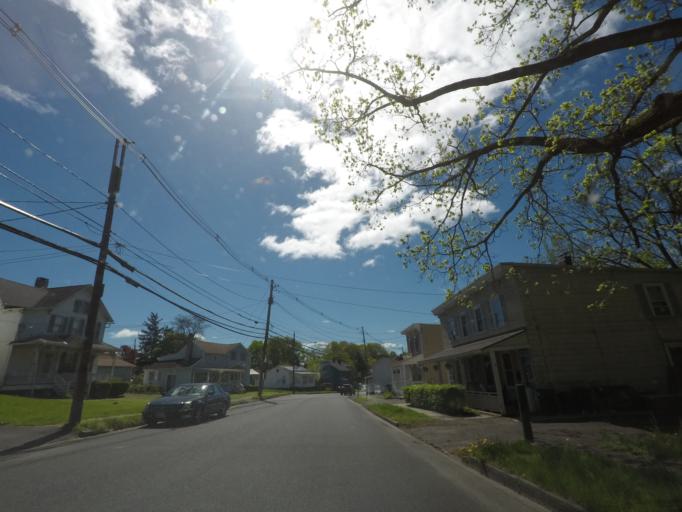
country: US
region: New York
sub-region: Ulster County
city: Saugerties
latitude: 42.0743
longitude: -73.9531
